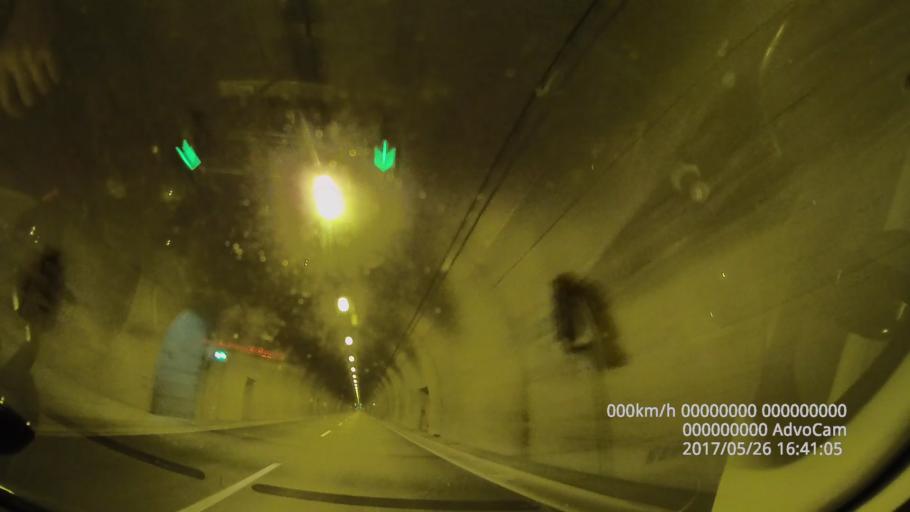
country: GR
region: Central Greece
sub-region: Nomos Fthiotidos
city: Rodhitsa
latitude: 38.9038
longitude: 22.5332
